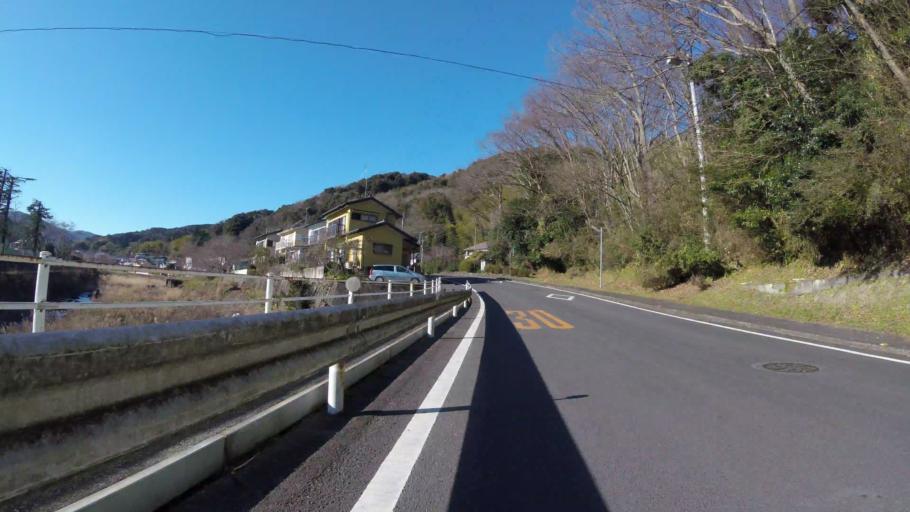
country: JP
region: Shizuoka
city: Heda
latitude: 34.9702
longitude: 138.9186
